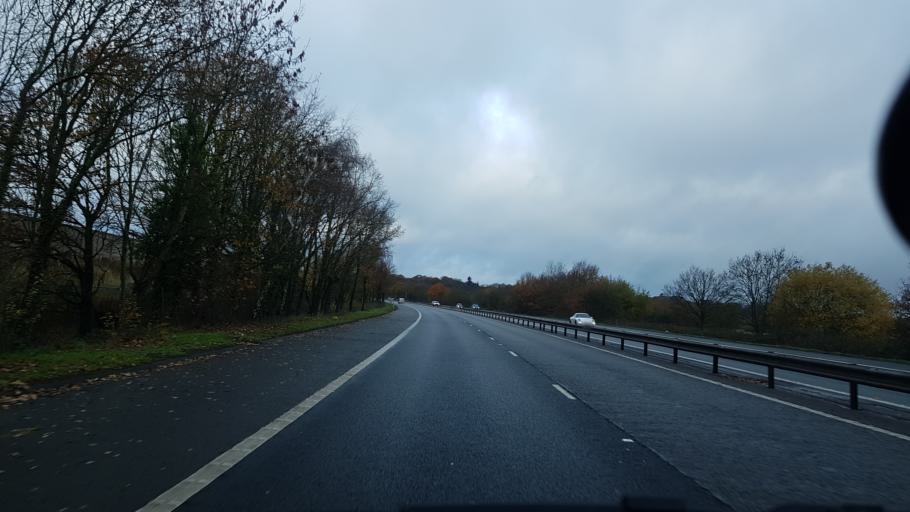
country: GB
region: England
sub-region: Wokingham
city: Wokingham
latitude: 51.4230
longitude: -0.8164
